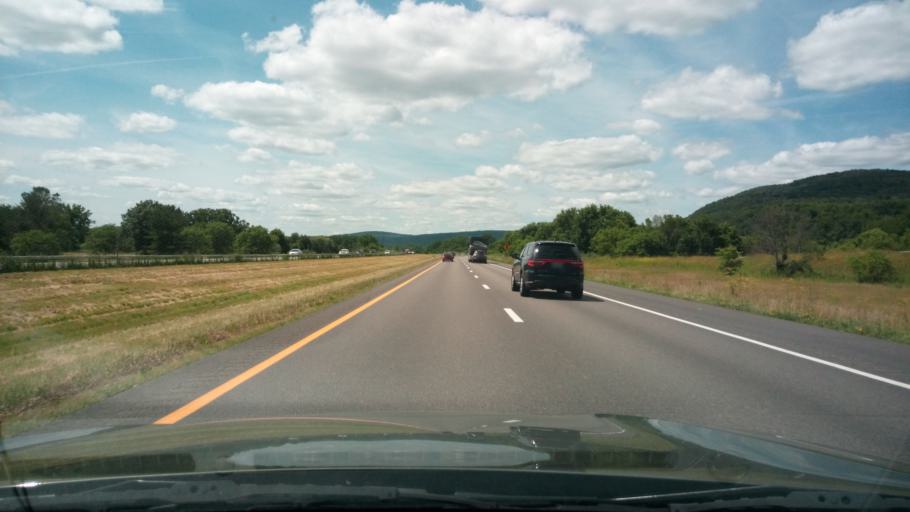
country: US
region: Pennsylvania
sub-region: Bradford County
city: South Waverly
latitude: 42.0075
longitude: -76.6290
